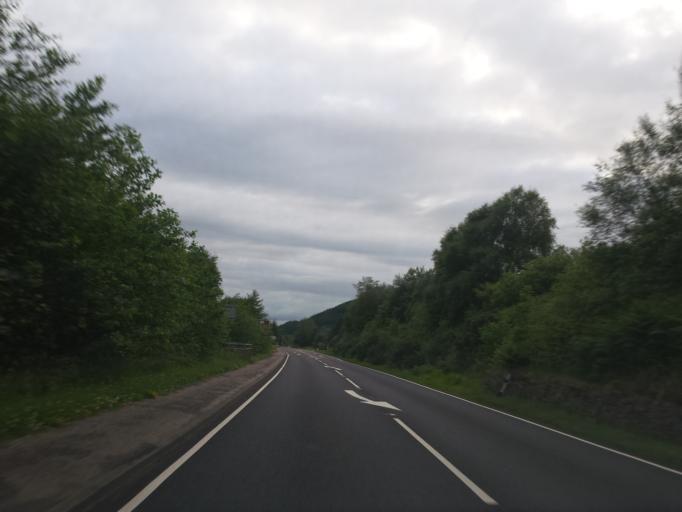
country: GB
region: Scotland
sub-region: Highland
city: Portree
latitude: 57.2855
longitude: -5.5771
